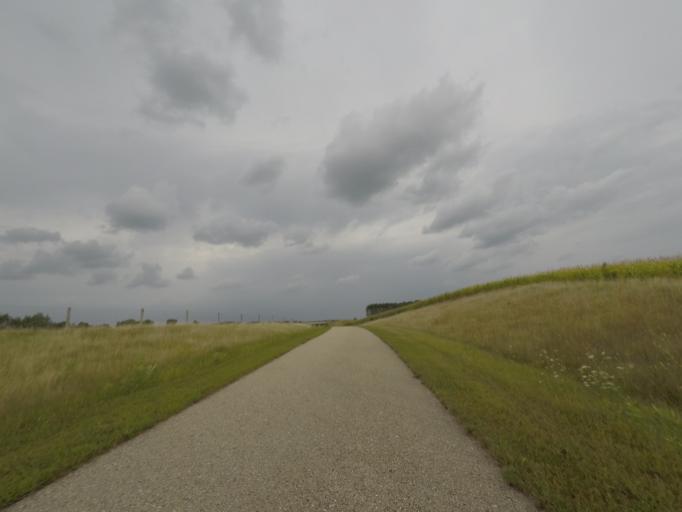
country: US
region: Wisconsin
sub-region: Jefferson County
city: Jefferson
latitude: 42.9812
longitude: -88.8253
